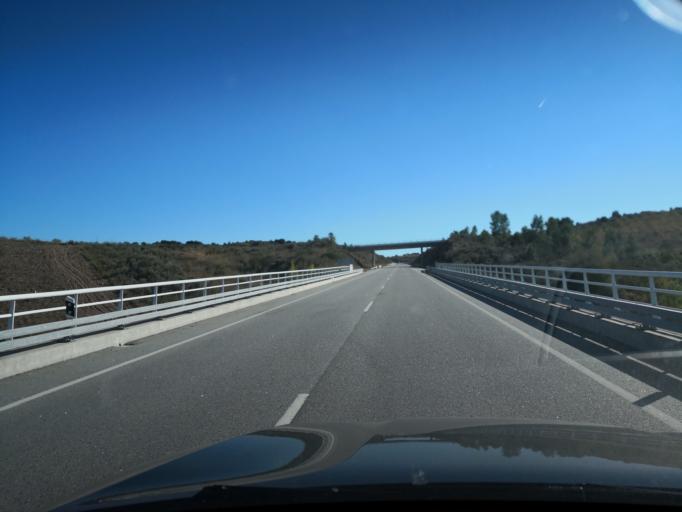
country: PT
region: Braganca
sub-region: Mirandela
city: Mirandela
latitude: 41.5097
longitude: -7.2283
